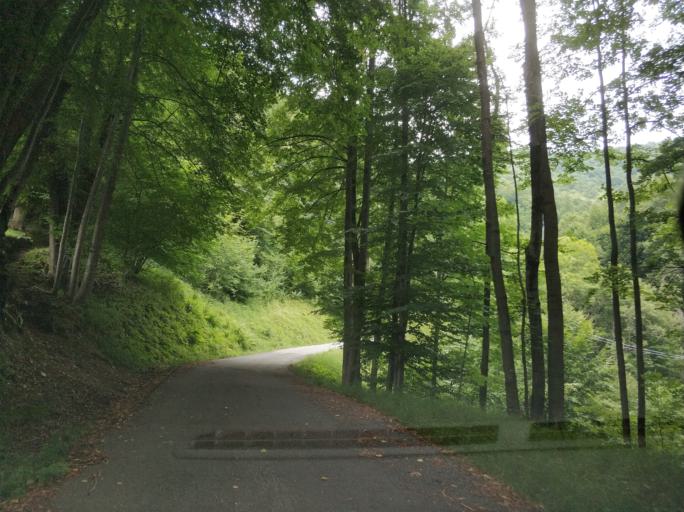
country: IT
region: Piedmont
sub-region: Provincia di Torino
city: Viu
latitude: 45.2171
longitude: 7.3929
